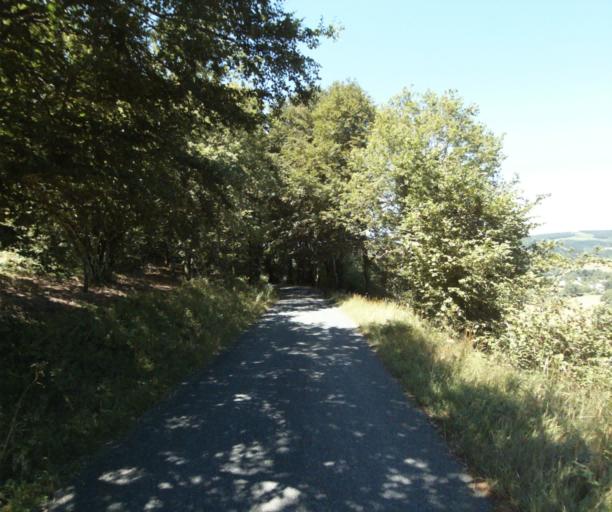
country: FR
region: Midi-Pyrenees
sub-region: Departement du Tarn
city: Dourgne
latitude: 43.4252
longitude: 2.1787
